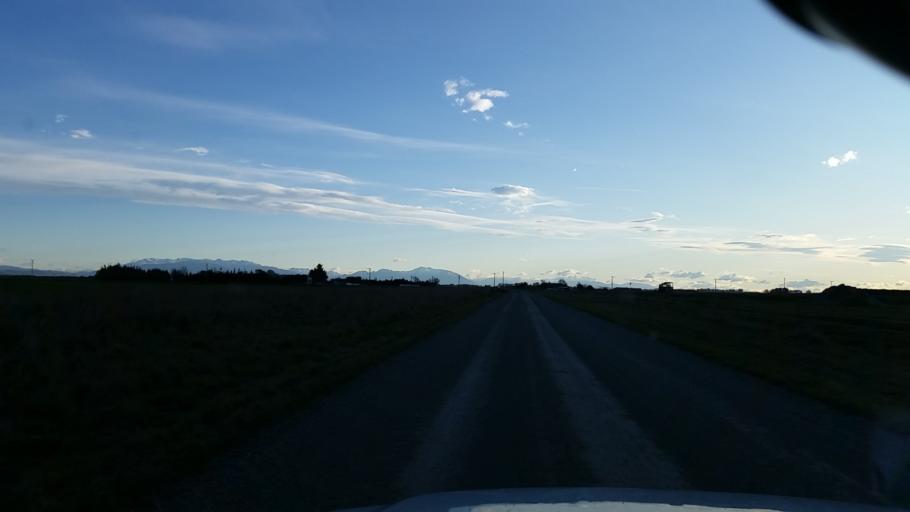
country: NZ
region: Canterbury
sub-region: Ashburton District
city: Tinwald
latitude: -43.9793
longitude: 171.5076
